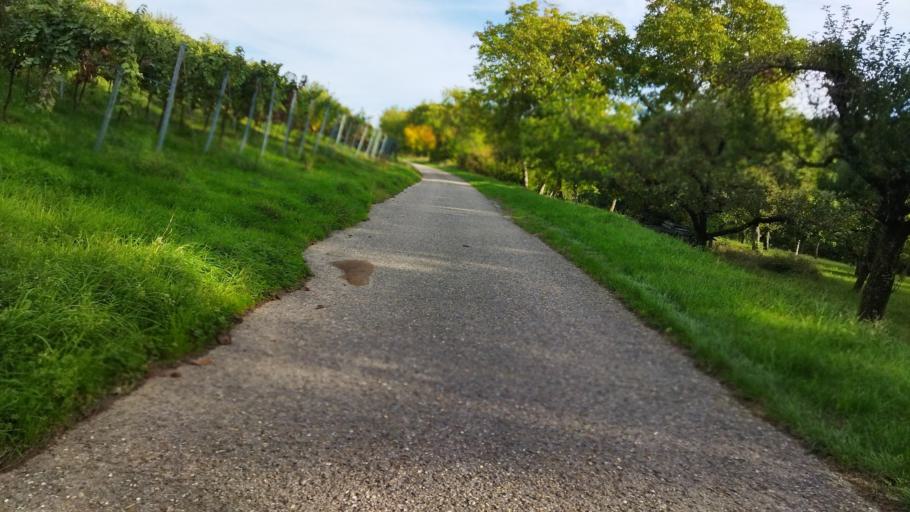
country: DE
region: Baden-Wuerttemberg
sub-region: Karlsruhe Region
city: Kurnbach
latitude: 49.0695
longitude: 8.8586
